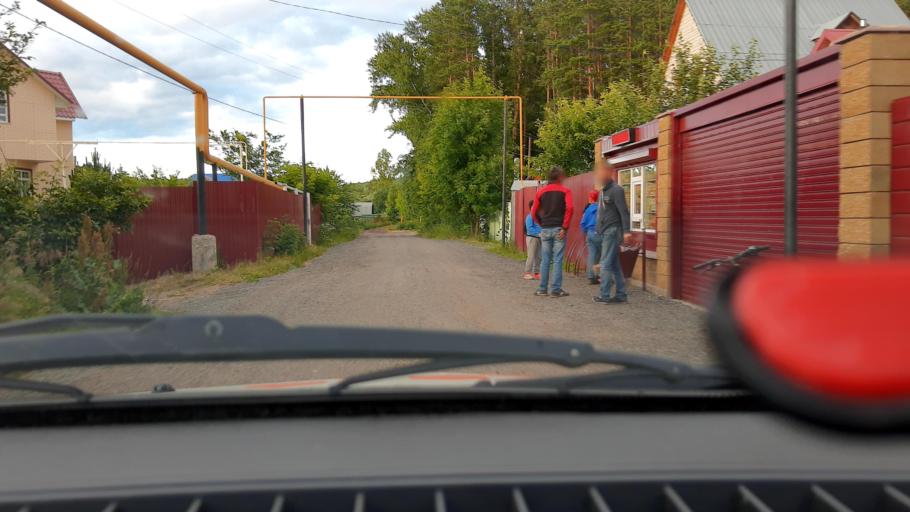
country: RU
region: Bashkortostan
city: Ufa
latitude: 54.6749
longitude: 55.8587
